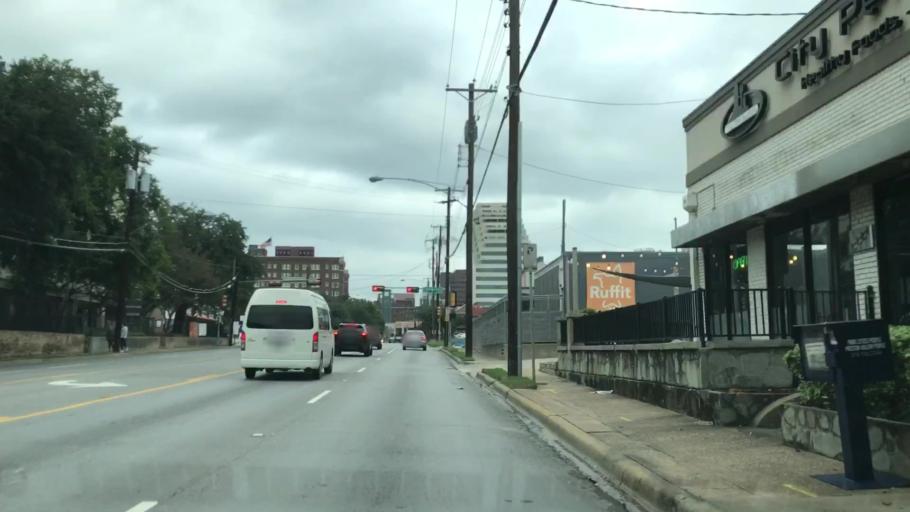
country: US
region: Texas
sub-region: Dallas County
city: Dallas
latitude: 32.8064
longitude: -96.8115
